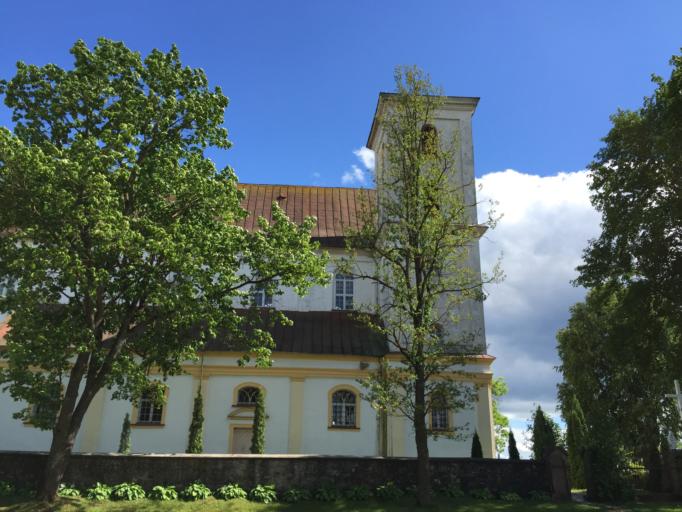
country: LT
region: Panevezys
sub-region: Birzai
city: Birzai
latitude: 56.3806
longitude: 24.6427
